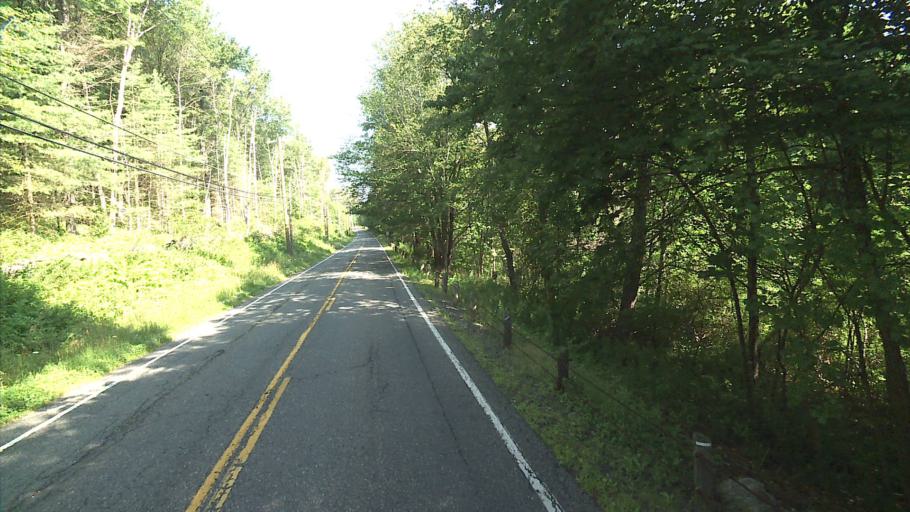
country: US
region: Connecticut
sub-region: Litchfield County
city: Winsted
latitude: 42.0005
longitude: -73.1030
